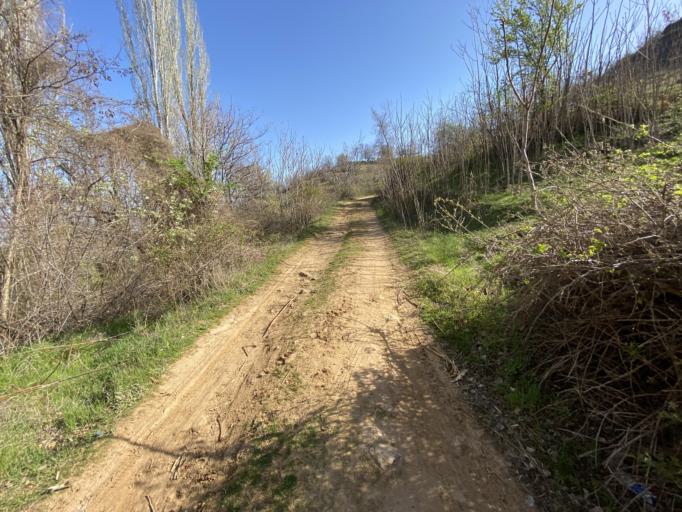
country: MK
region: Zrnovci
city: Zrnovci
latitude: 41.8453
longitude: 22.4185
